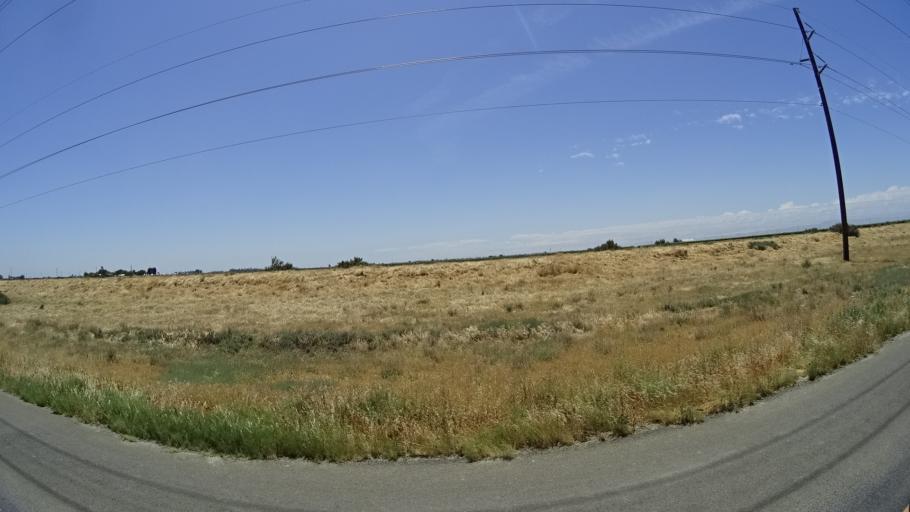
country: US
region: California
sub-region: Kings County
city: Stratford
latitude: 36.2406
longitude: -119.8232
